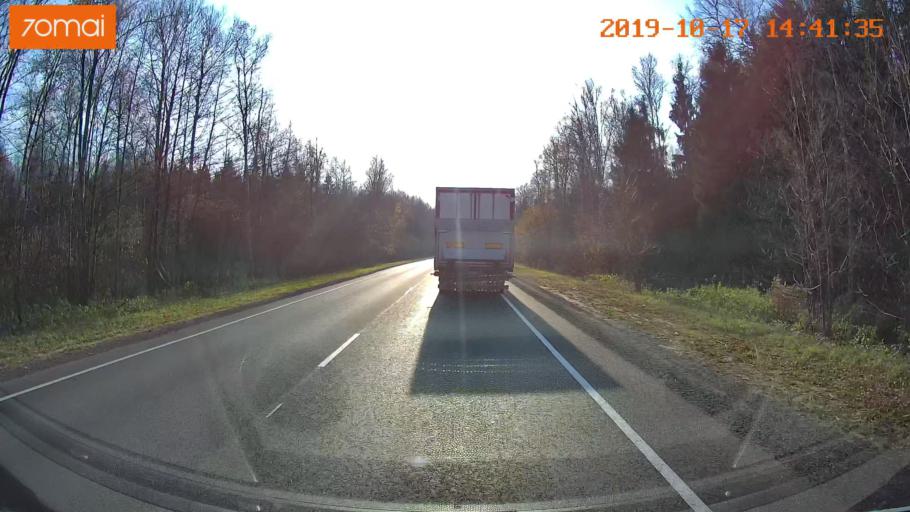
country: RU
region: Rjazan
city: Solotcha
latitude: 54.8440
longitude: 39.9379
